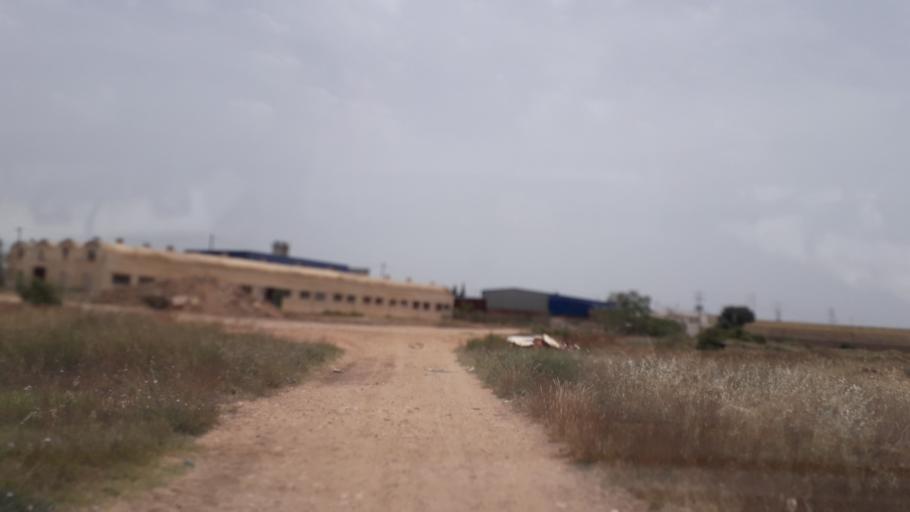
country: TN
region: Safaqis
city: Al Qarmadah
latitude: 34.8465
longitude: 10.7576
